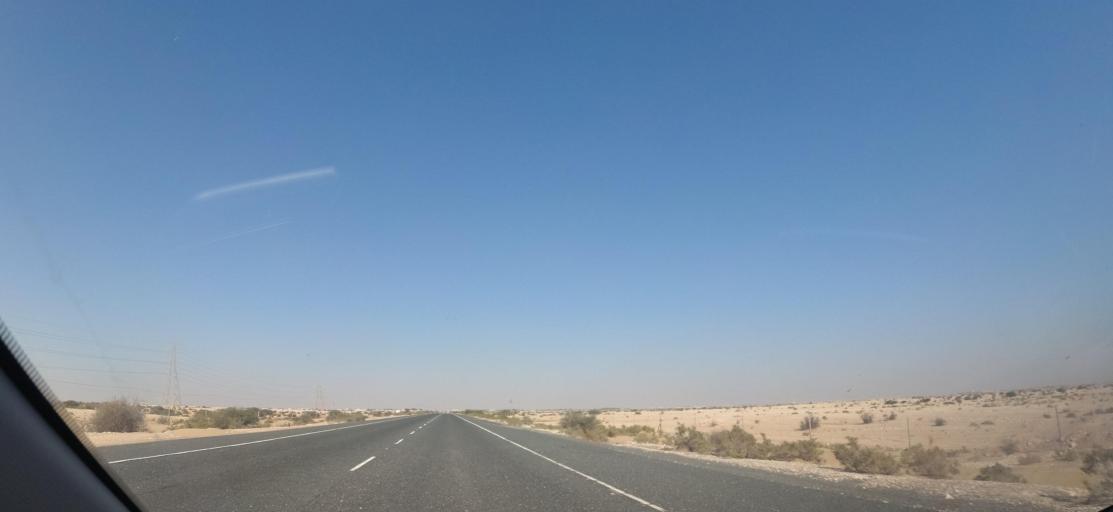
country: QA
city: Al Jumayliyah
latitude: 25.5907
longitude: 51.0642
